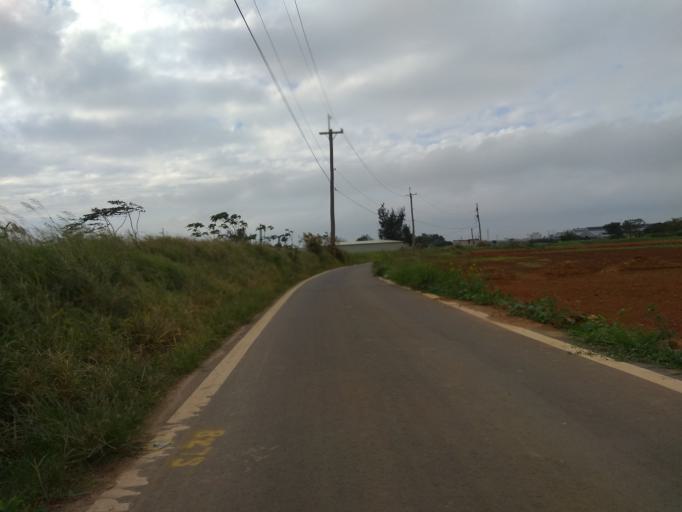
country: TW
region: Taiwan
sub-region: Hsinchu
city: Zhubei
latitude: 24.9765
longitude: 121.0394
